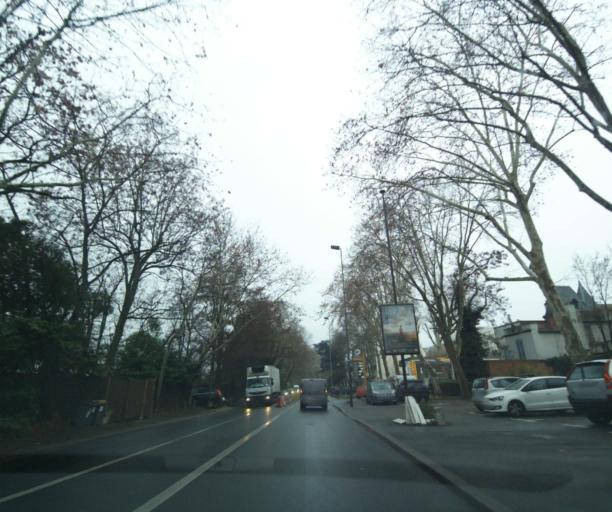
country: FR
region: Ile-de-France
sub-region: Departement des Hauts-de-Seine
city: Suresnes
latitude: 48.8556
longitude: 2.2230
